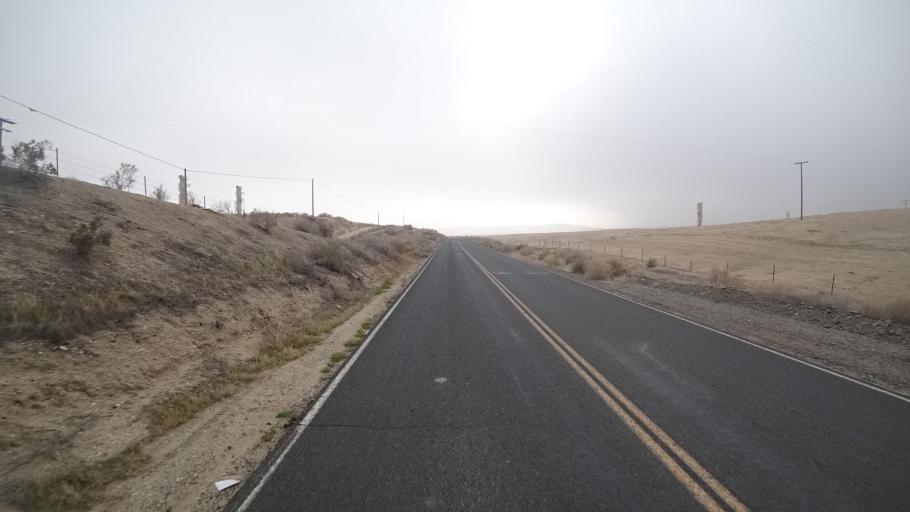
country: US
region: California
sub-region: Kern County
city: Ford City
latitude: 35.2583
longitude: -119.4624
